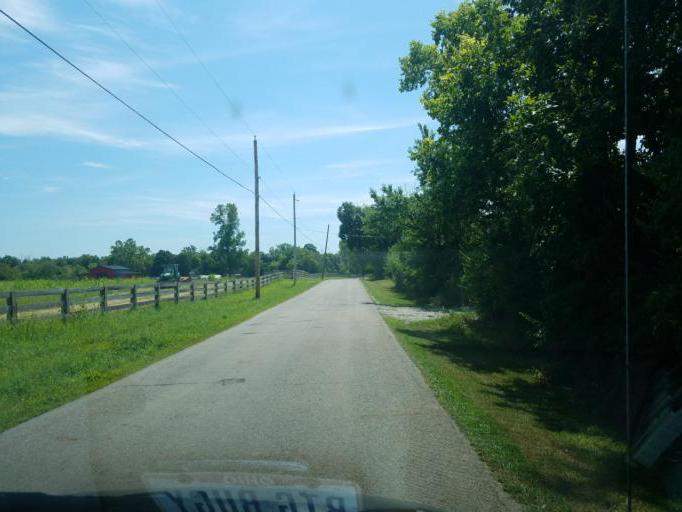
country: US
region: Ohio
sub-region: Franklin County
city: Grove City
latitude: 39.8552
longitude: -83.1941
